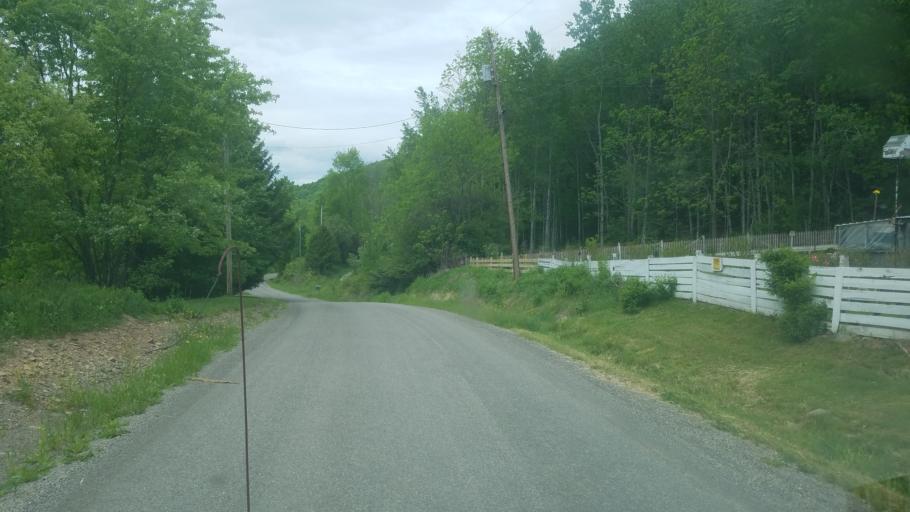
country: US
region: Pennsylvania
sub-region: Tioga County
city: Westfield
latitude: 41.8867
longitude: -77.5982
